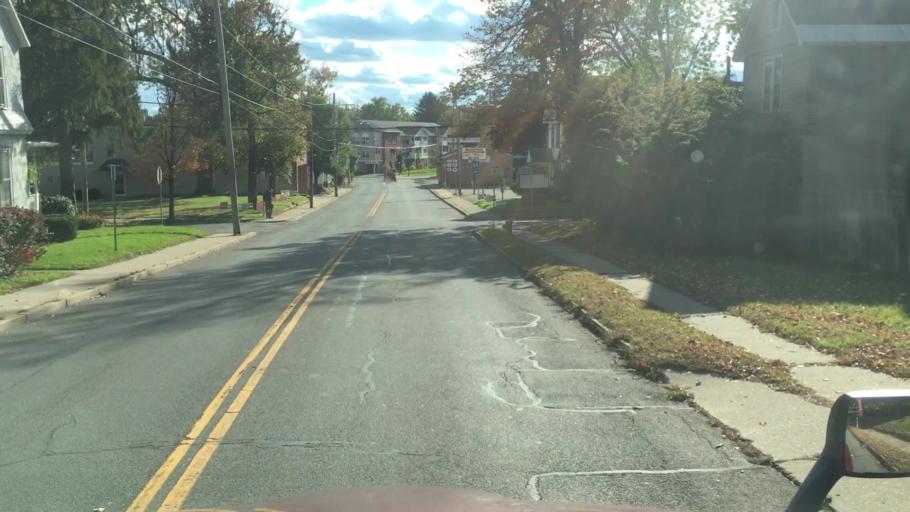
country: US
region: New York
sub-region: Schenectady County
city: Scotia
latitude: 42.8268
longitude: -73.9611
